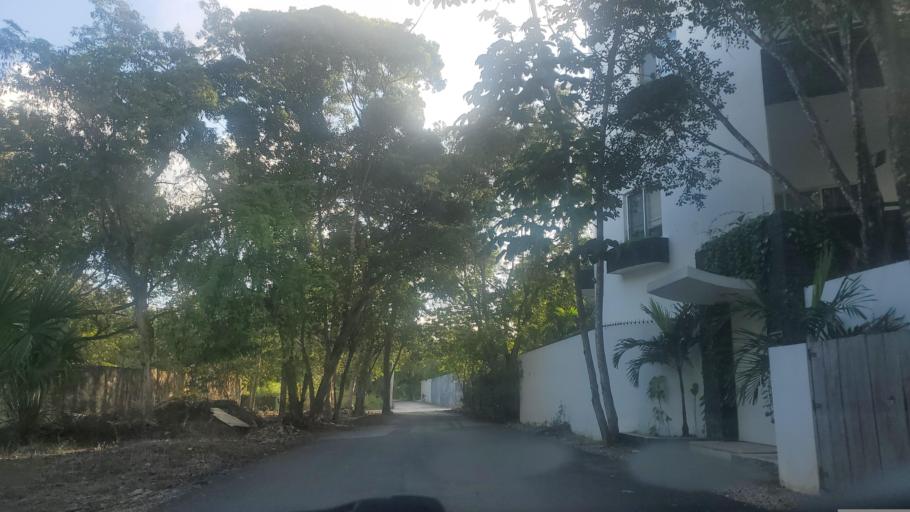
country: MX
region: Quintana Roo
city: Tulum
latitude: 20.2092
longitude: -87.4758
